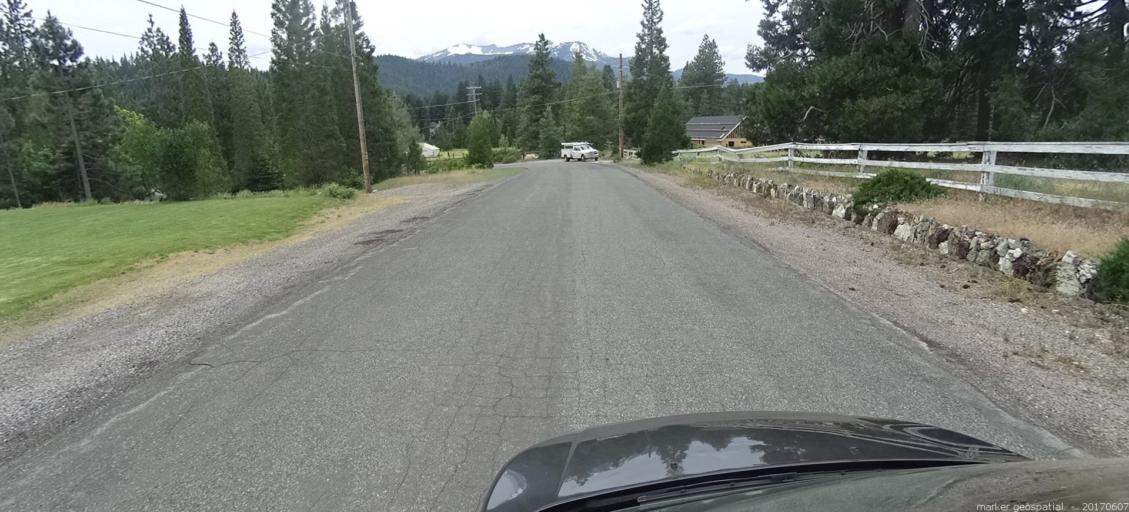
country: US
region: California
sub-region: Siskiyou County
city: Mount Shasta
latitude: 41.3344
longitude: -122.3437
